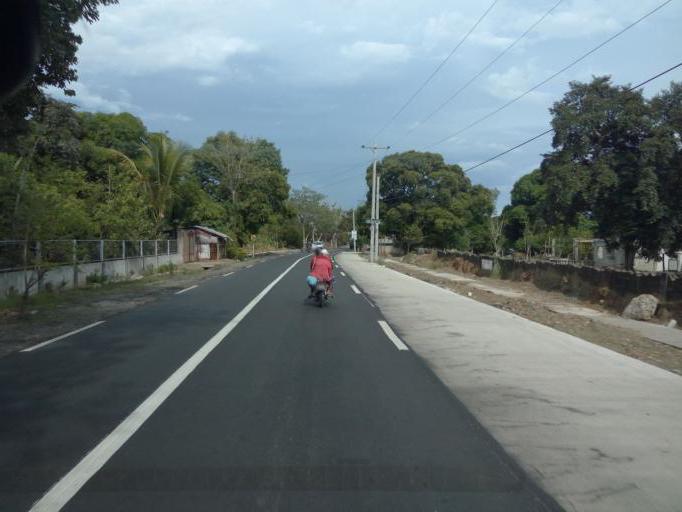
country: PH
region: Central Luzon
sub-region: Province of Nueva Ecija
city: Parista
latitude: 15.8267
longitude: 120.9491
